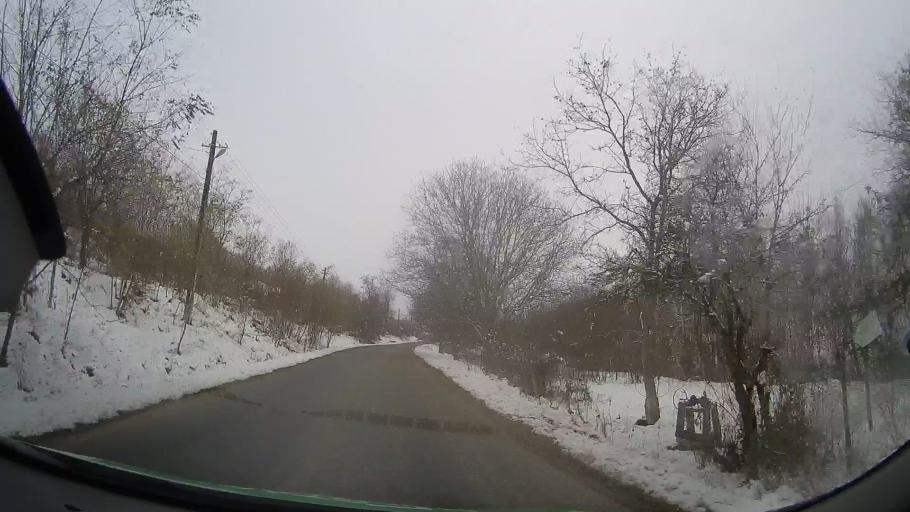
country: RO
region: Bacau
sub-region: Comuna Vultureni
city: Vultureni
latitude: 46.3860
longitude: 27.2779
